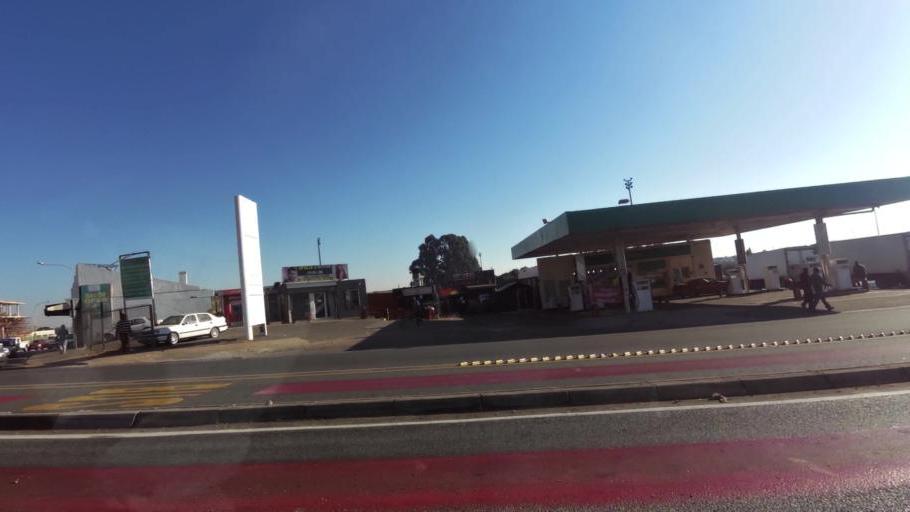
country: ZA
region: Gauteng
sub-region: City of Johannesburg Metropolitan Municipality
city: Johannesburg
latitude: -26.1860
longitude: 27.9839
